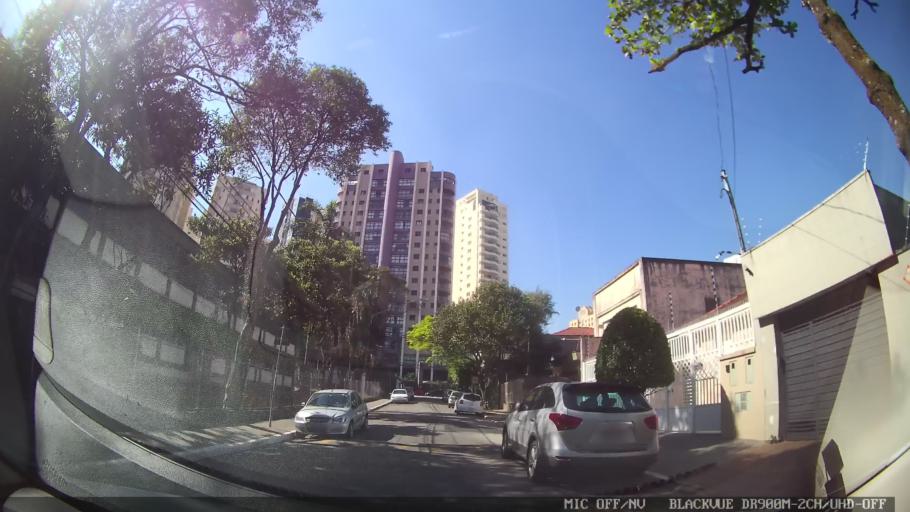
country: BR
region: Sao Paulo
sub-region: Sao Paulo
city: Sao Paulo
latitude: -23.5092
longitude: -46.6629
